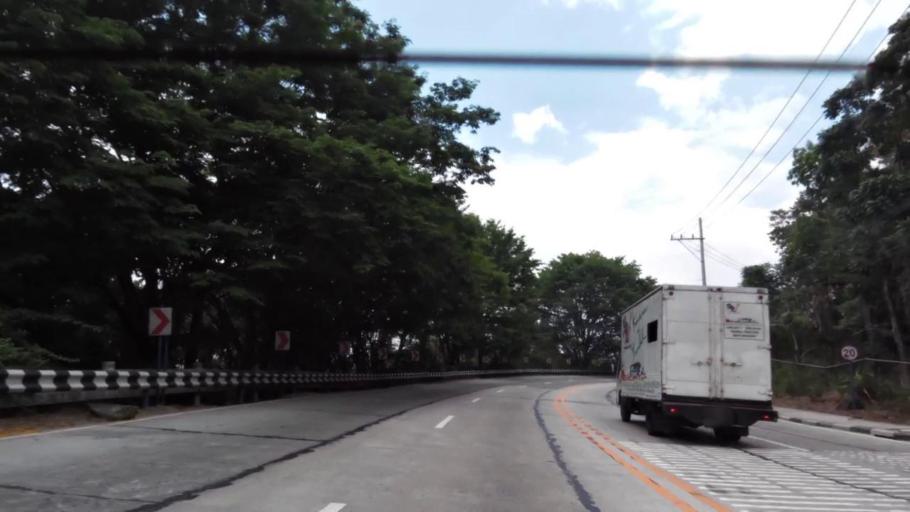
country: PH
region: Calabarzon
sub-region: Province of Rizal
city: Antipolo
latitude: 14.6145
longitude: 121.1514
